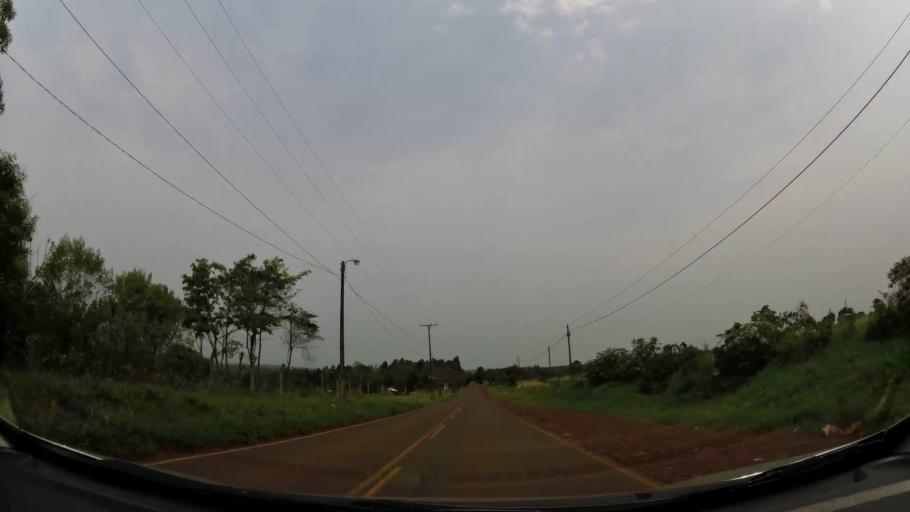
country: AR
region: Misiones
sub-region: Departamento de Iguazu
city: Puerto Iguazu
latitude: -25.5811
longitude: -54.6029
